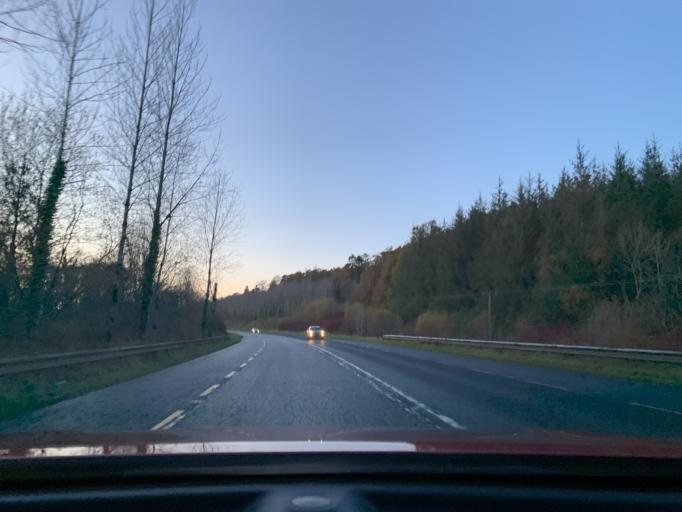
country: IE
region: Connaught
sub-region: County Leitrim
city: Carrick-on-Shannon
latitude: 53.9356
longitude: -8.0099
